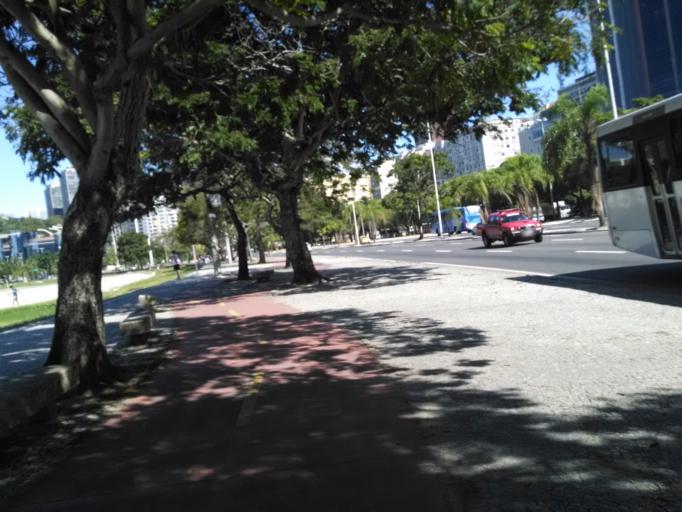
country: BR
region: Rio de Janeiro
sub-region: Rio De Janeiro
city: Rio de Janeiro
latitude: -22.9455
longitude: -43.1815
